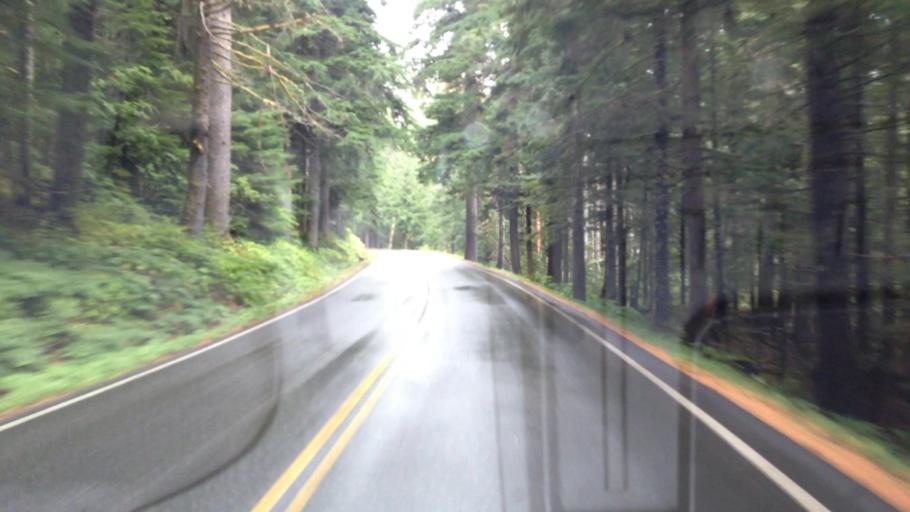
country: US
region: Washington
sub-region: Pierce County
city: Eatonville
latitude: 46.7398
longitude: -121.8264
